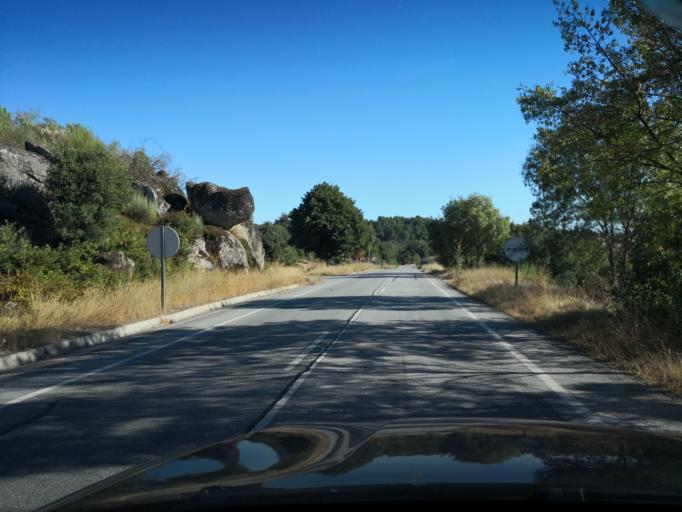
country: PT
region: Vila Real
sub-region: Valpacos
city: Valpacos
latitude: 41.6429
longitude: -7.3183
